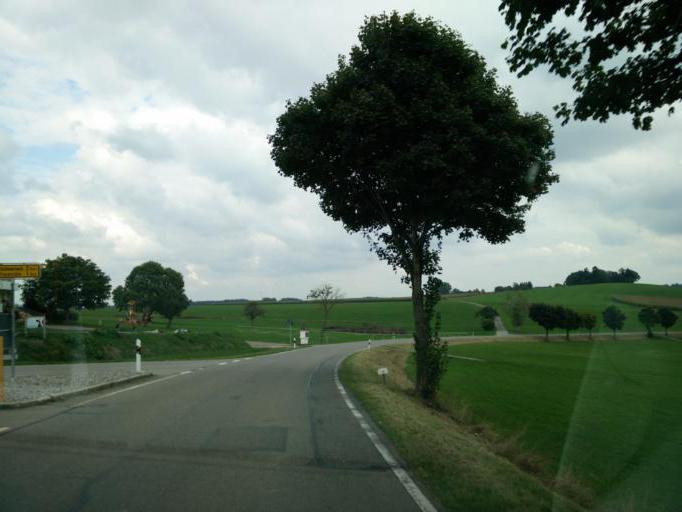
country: DE
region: Baden-Wuerttemberg
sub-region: Tuebingen Region
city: Bad Wurzach
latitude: 47.9476
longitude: 9.9159
